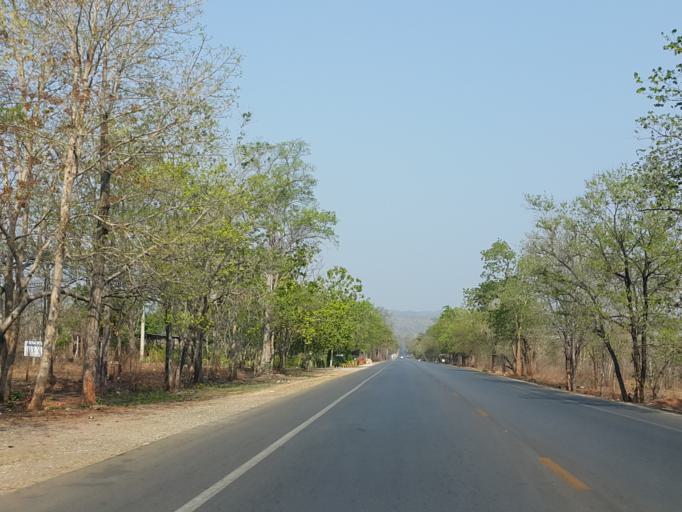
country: TH
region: Kanchanaburi
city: Sai Yok
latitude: 14.0948
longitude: 99.2592
